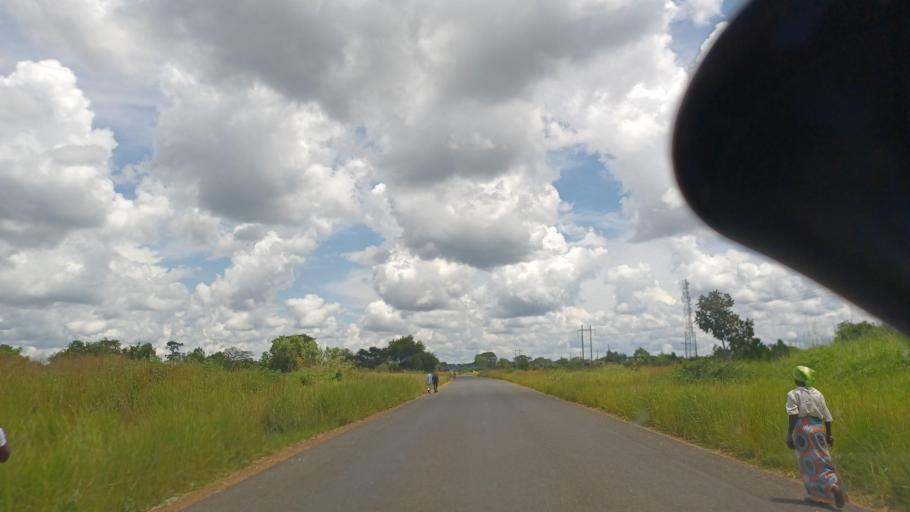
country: ZM
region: North-Western
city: Solwezi
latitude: -12.4189
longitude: 26.2256
